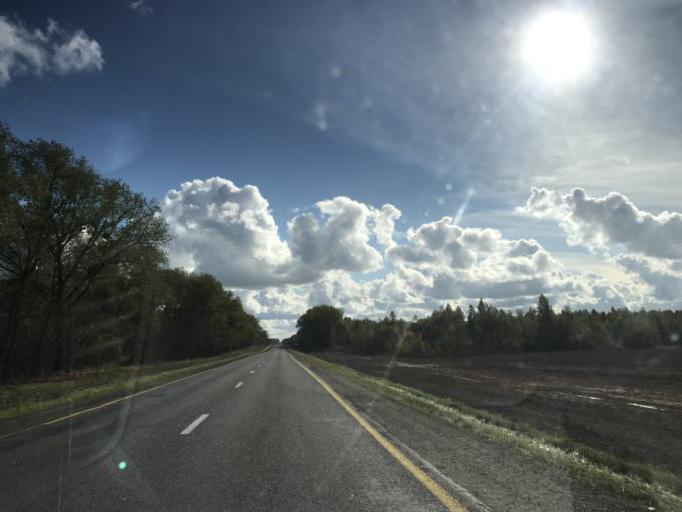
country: BY
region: Gomel
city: Buda-Kashalyova
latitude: 52.7850
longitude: 30.7464
